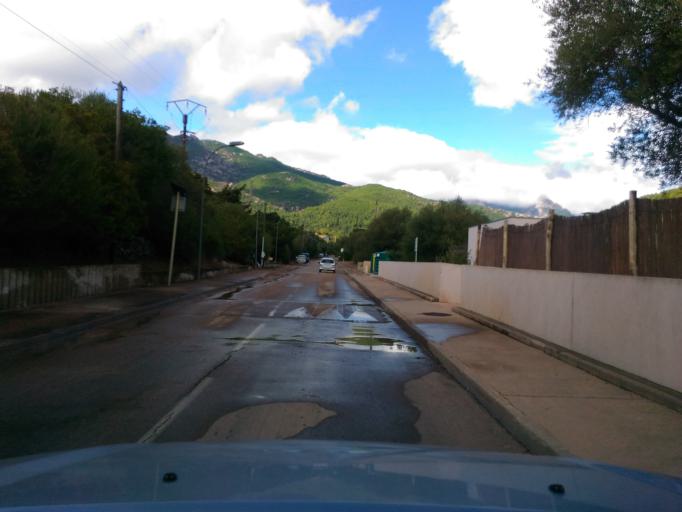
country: FR
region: Corsica
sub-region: Departement de la Corse-du-Sud
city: Porto-Vecchio
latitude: 41.7074
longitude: 9.3168
